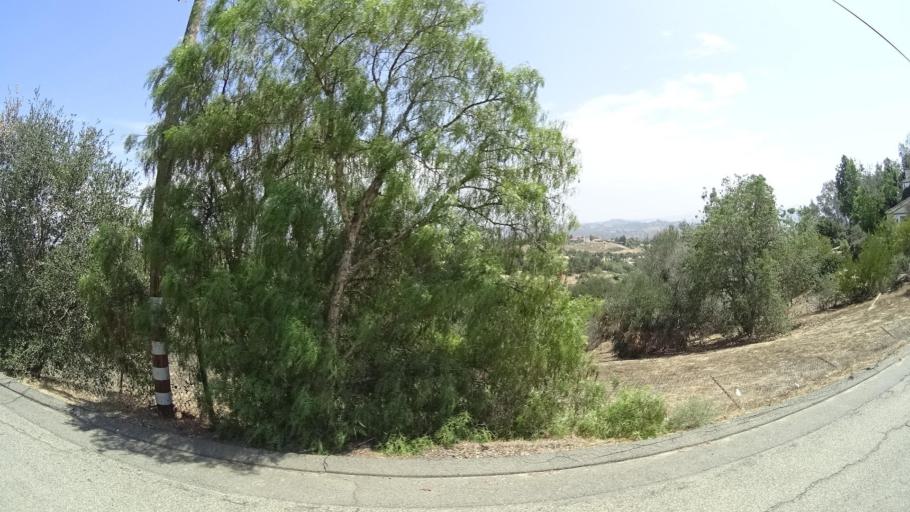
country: US
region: California
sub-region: San Diego County
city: Bonsall
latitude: 33.3118
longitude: -117.2243
